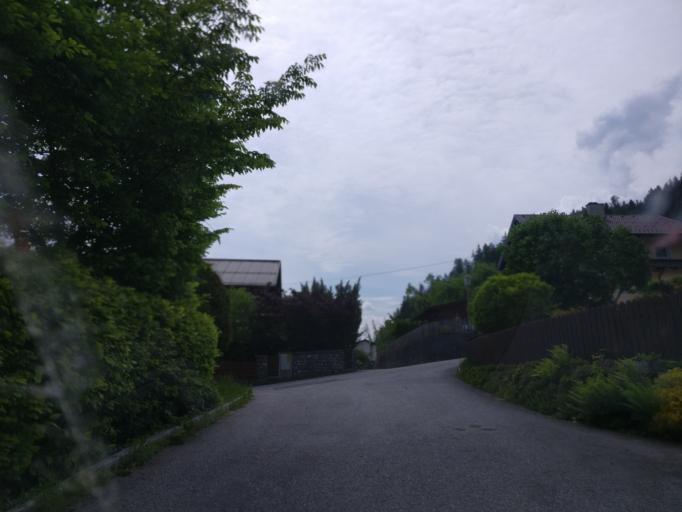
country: AT
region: Salzburg
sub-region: Politischer Bezirk Sankt Johann im Pongau
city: Werfen
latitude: 47.4783
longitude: 13.1848
